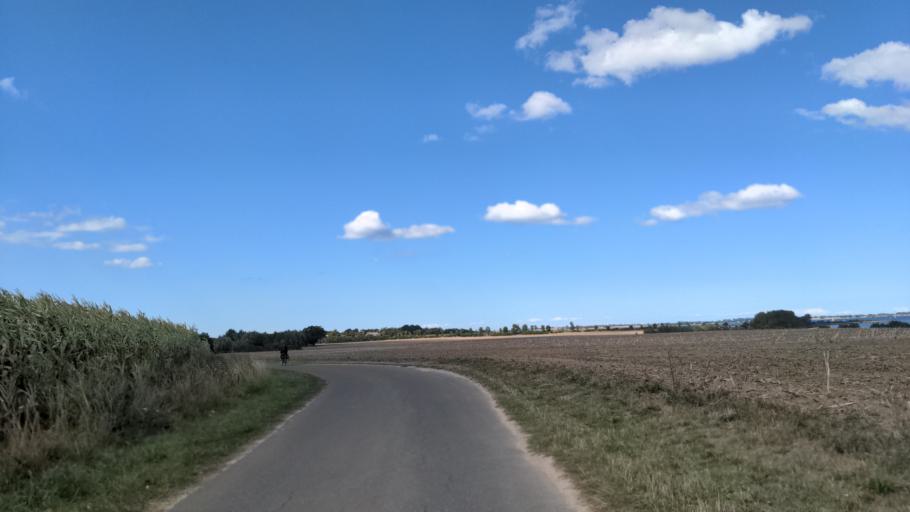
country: DE
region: Mecklenburg-Vorpommern
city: Wismar
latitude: 53.9198
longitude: 11.3983
